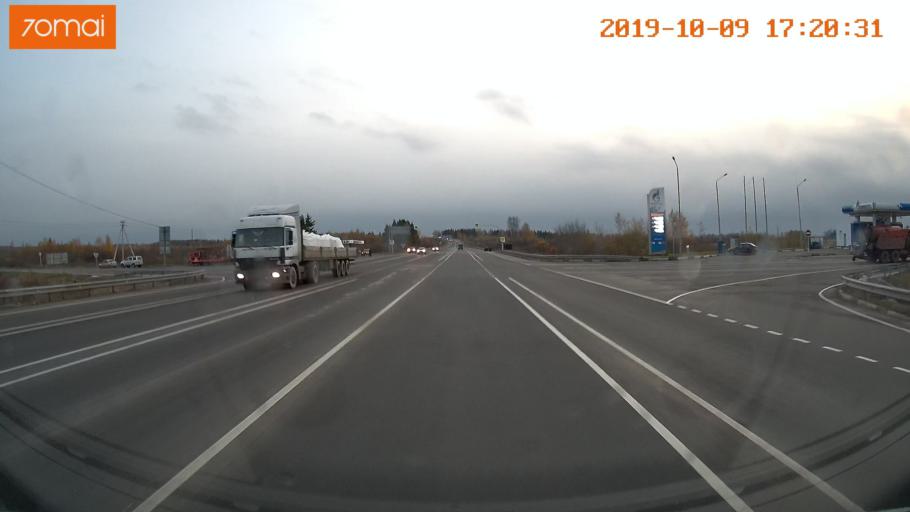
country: RU
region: Ivanovo
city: Furmanov
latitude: 57.2338
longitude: 41.1406
